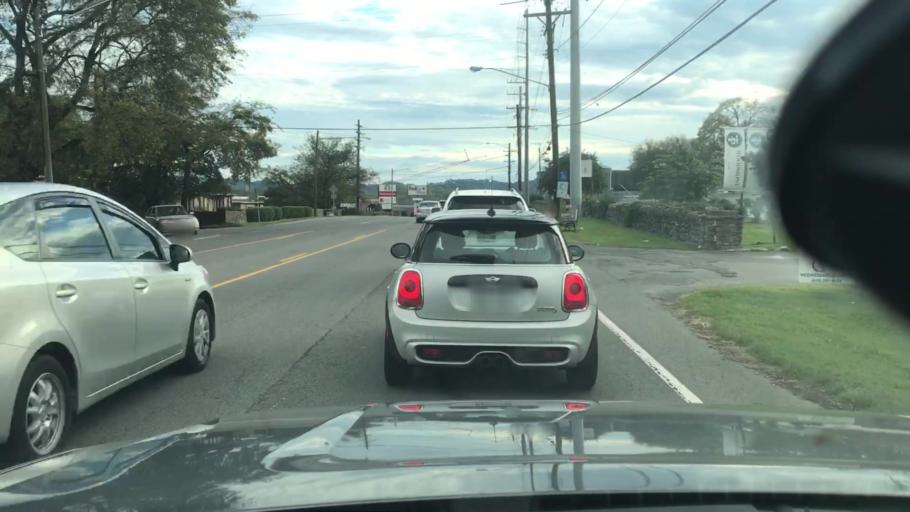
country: US
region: Tennessee
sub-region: Davidson County
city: Oak Hill
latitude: 36.1116
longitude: -86.8113
